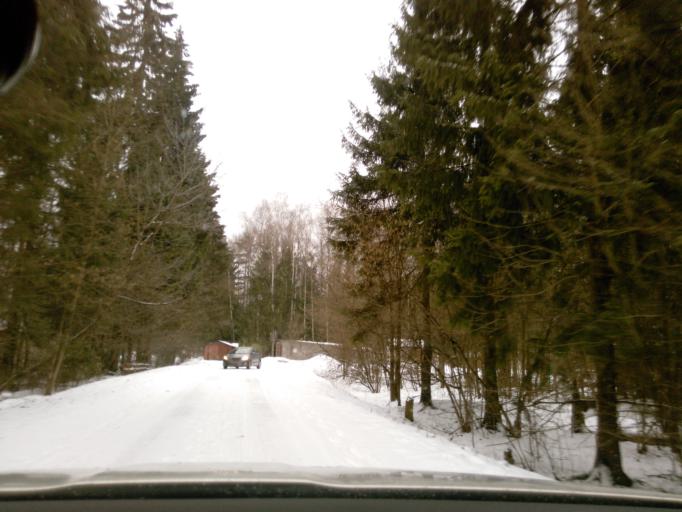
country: RU
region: Moskovskaya
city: Skhodnya
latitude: 55.9694
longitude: 37.2834
